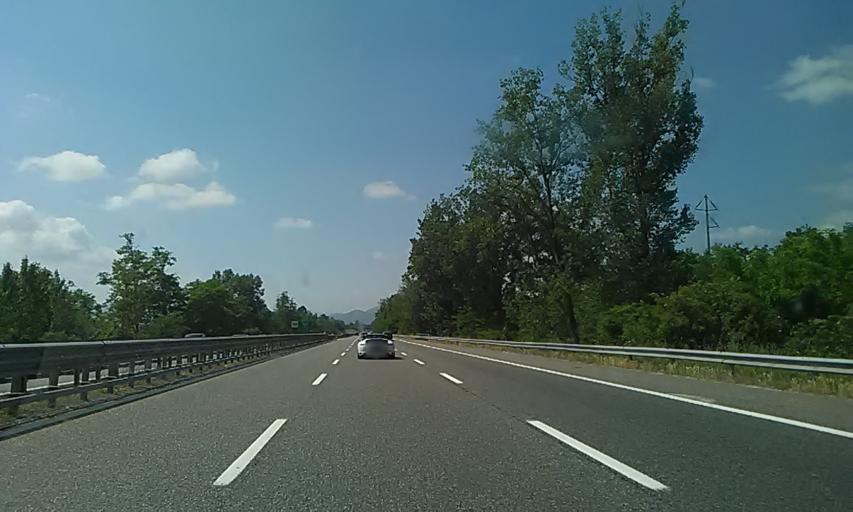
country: IT
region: Piedmont
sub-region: Provincia di Alessandria
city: Silvano d'Orba
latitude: 44.7002
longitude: 8.6669
